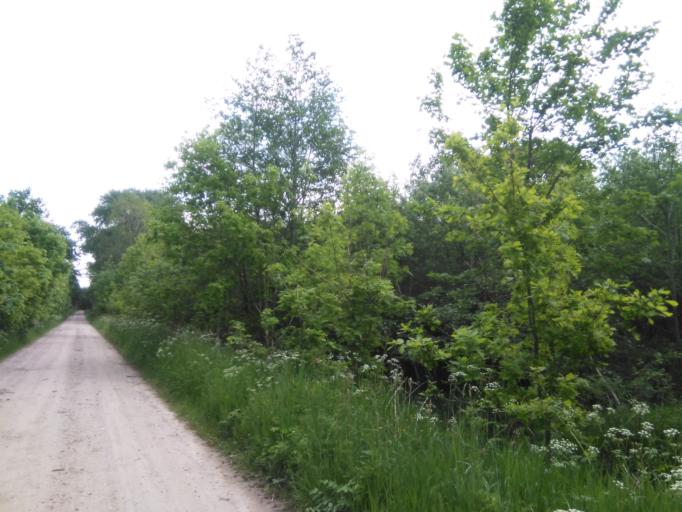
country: DK
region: Central Jutland
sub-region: Arhus Kommune
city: Sabro
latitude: 56.2765
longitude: 9.9693
